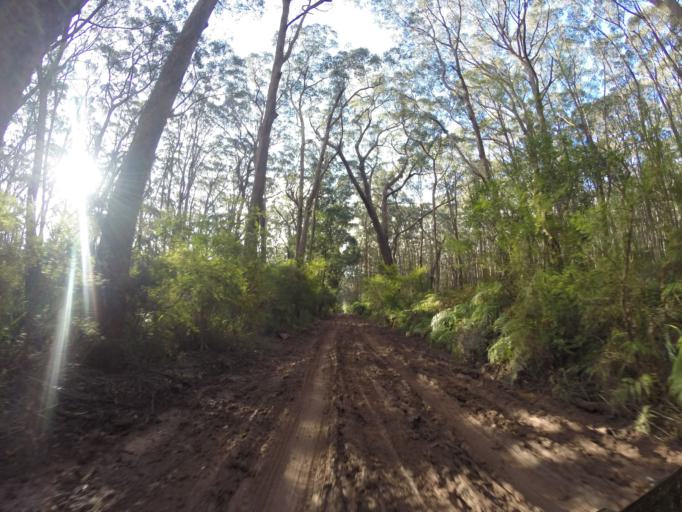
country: AU
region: New South Wales
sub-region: Wollongong
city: Cordeaux Heights
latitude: -34.4098
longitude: 150.7853
